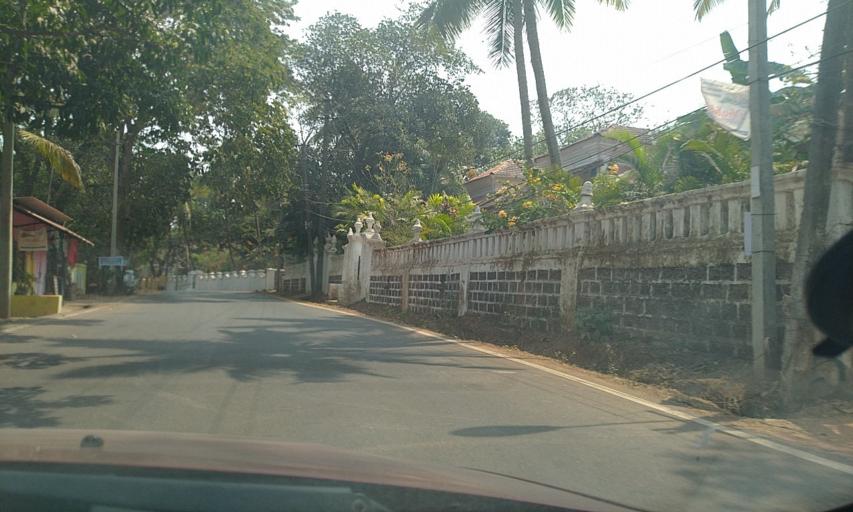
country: IN
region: Goa
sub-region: North Goa
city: Solim
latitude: 15.5927
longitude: 73.7759
